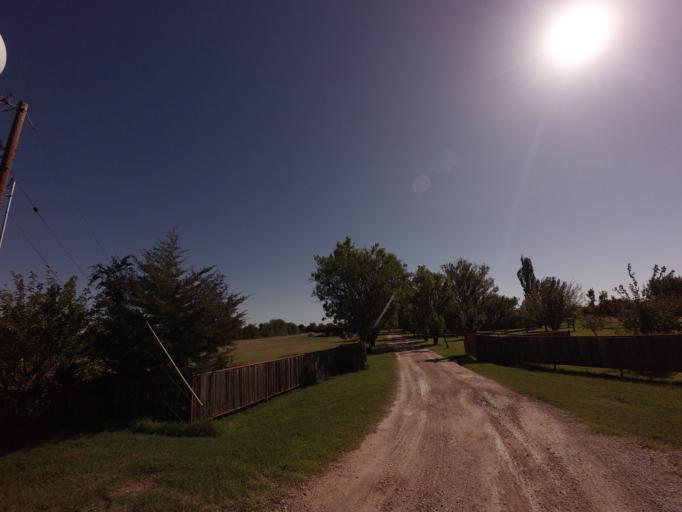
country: US
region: New Mexico
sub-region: Curry County
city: Clovis
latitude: 34.4310
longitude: -103.1876
